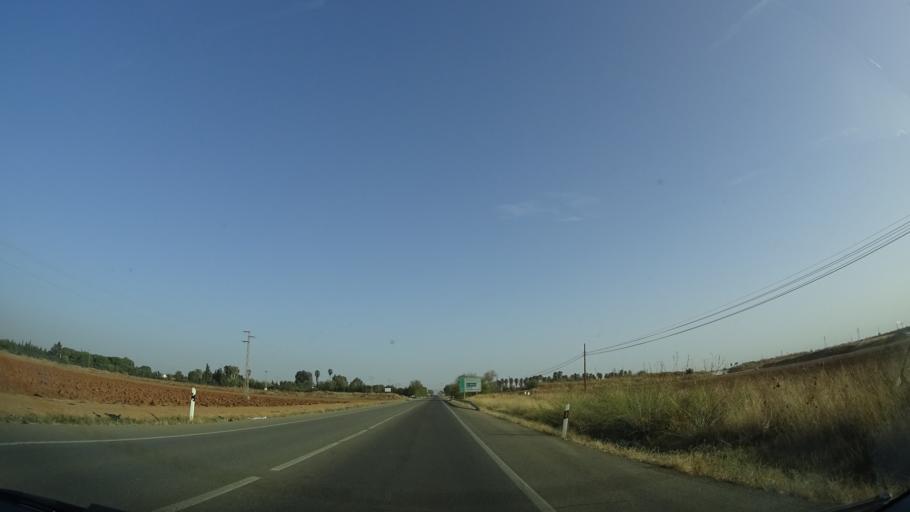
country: ES
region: Andalusia
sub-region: Provincia de Sevilla
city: La Algaba
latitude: 37.4380
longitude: -5.9789
